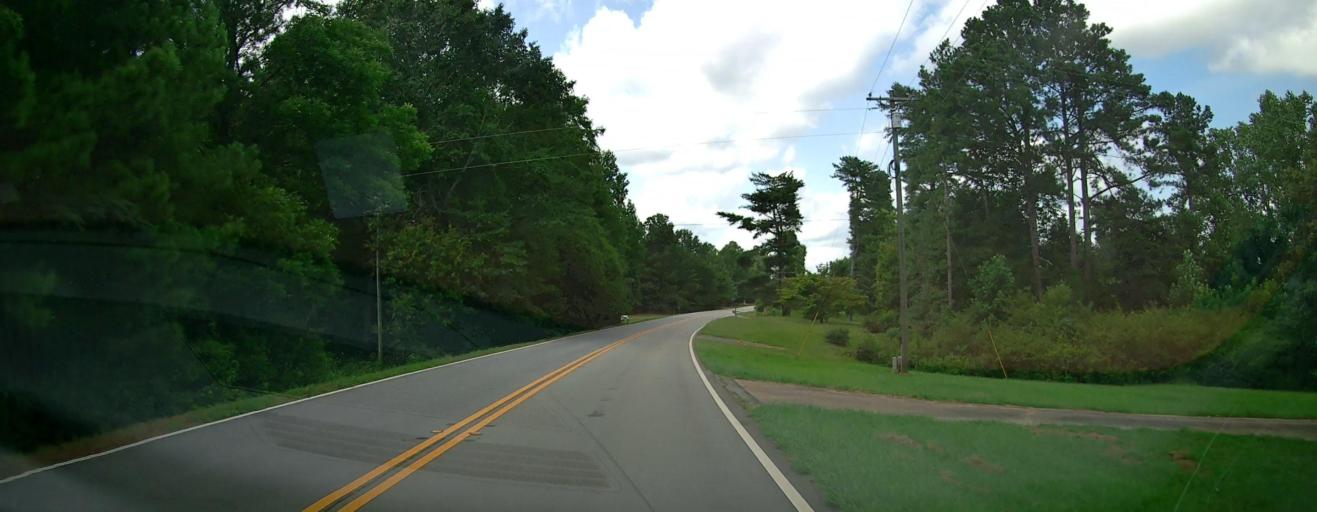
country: US
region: Georgia
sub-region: Carroll County
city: Bowdon
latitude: 33.4536
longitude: -85.2951
